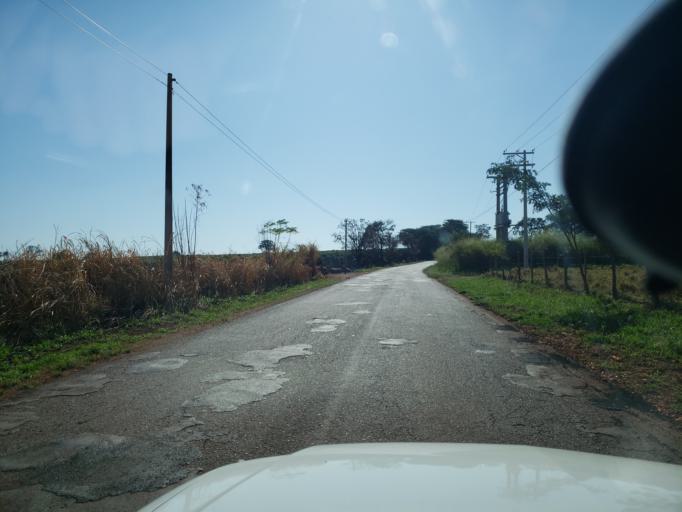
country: BR
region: Sao Paulo
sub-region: Moji-Guacu
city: Mogi-Gaucu
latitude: -22.3441
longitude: -46.8909
